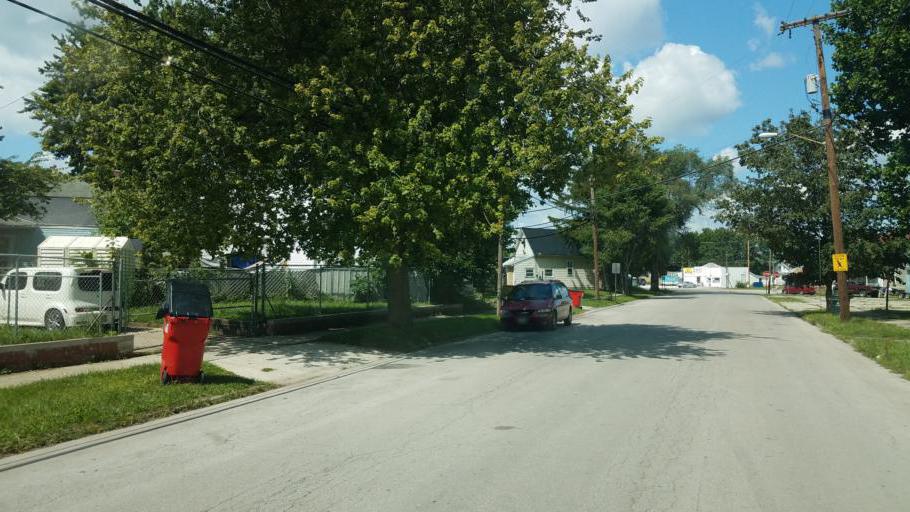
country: US
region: Ohio
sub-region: Seneca County
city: Fostoria
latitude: 41.1560
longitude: -83.4100
